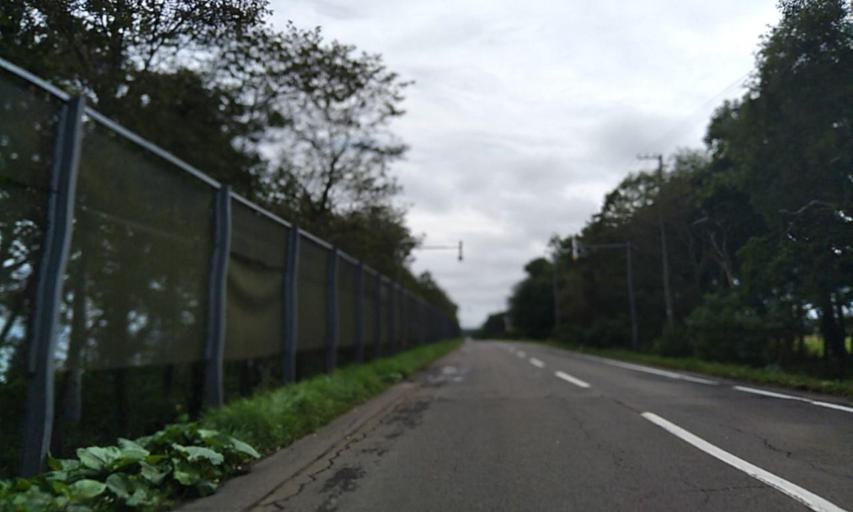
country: JP
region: Hokkaido
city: Shibetsu
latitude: 43.5949
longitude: 145.2005
